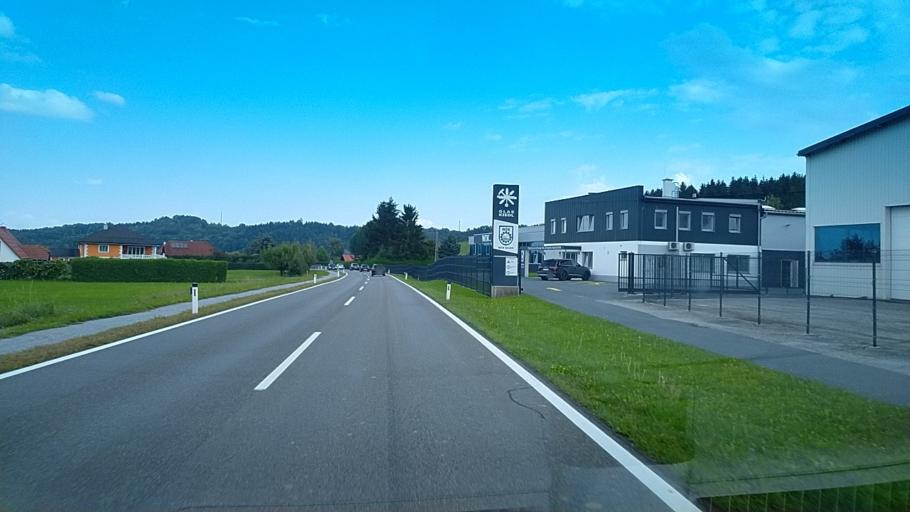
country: AT
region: Styria
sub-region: Politischer Bezirk Deutschlandsberg
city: Schwanberg
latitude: 46.7534
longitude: 15.2172
